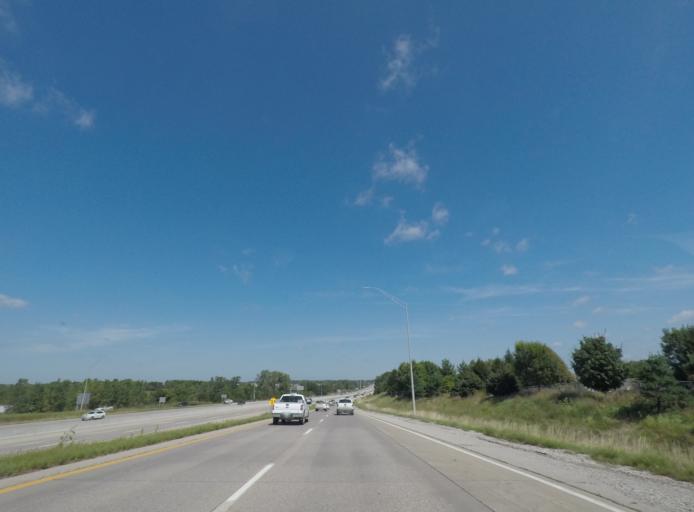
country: US
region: Iowa
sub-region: Polk County
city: Clive
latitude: 41.5613
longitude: -93.7761
